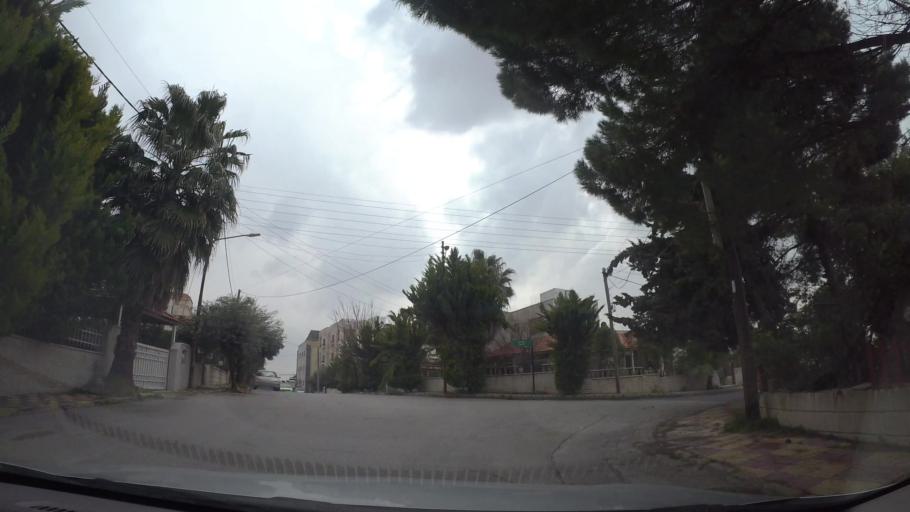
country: JO
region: Amman
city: Umm as Summaq
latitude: 31.8888
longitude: 35.8539
